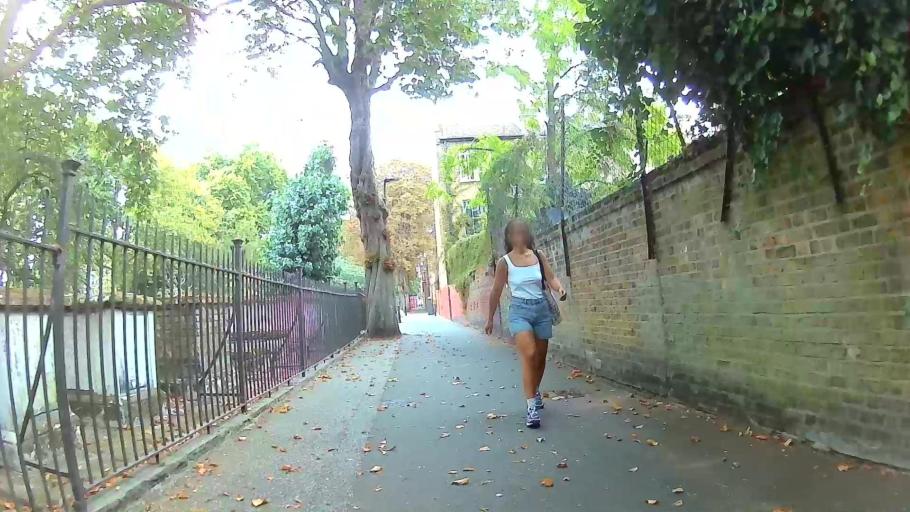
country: GB
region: England
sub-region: Greater London
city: Hackney
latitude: 51.5492
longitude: -0.0526
